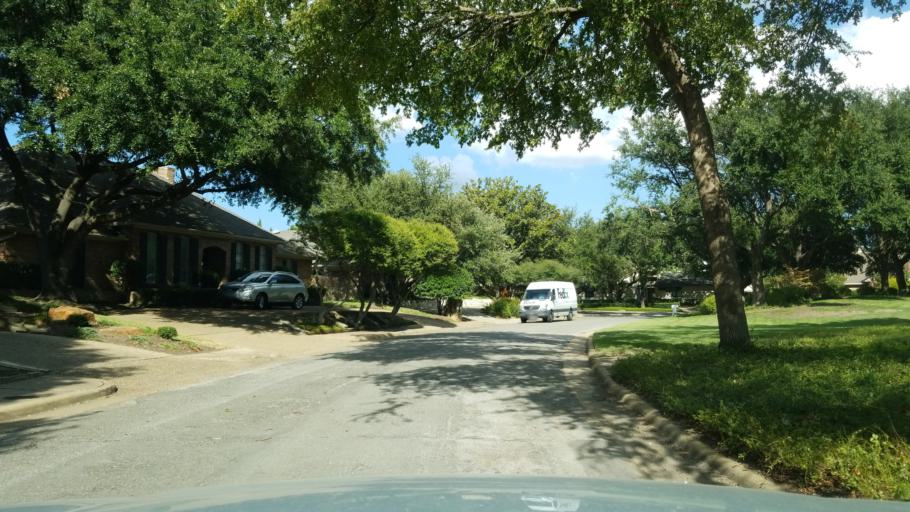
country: US
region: Texas
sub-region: Dallas County
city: Addison
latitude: 32.9628
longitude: -96.7992
